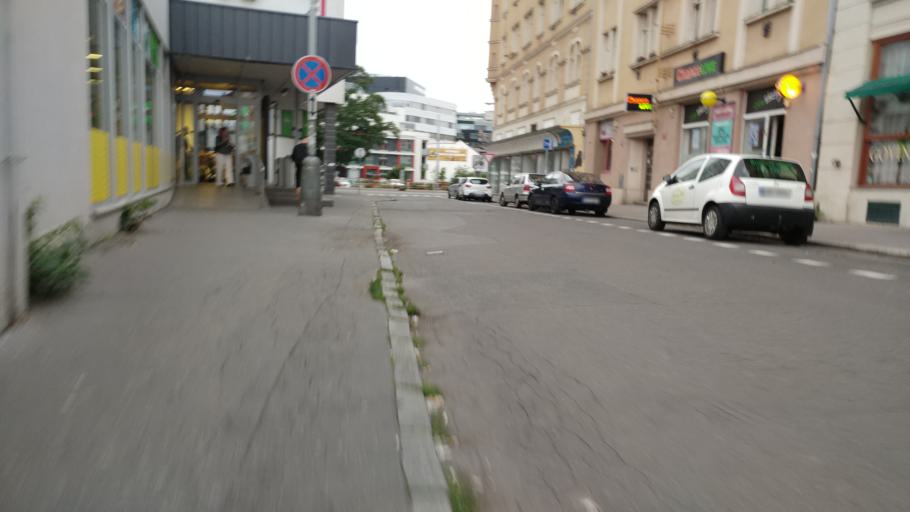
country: CZ
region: Praha
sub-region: Praha 8
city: Liben
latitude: 50.1051
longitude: 14.4739
